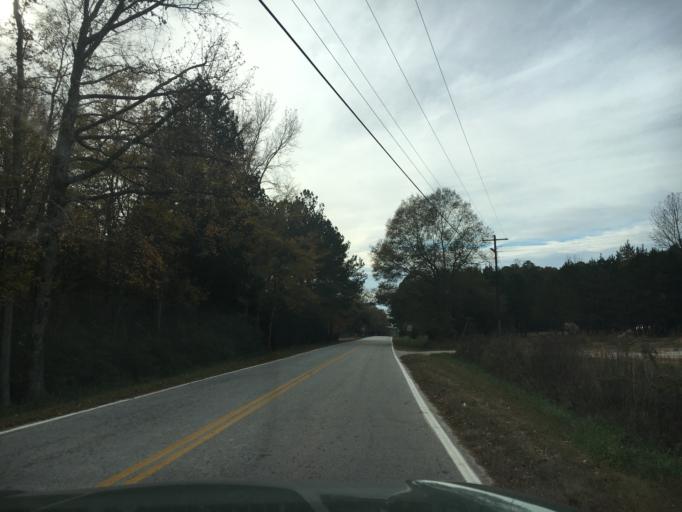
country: US
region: South Carolina
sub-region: Laurens County
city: Watts Mills
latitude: 34.4983
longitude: -81.9727
